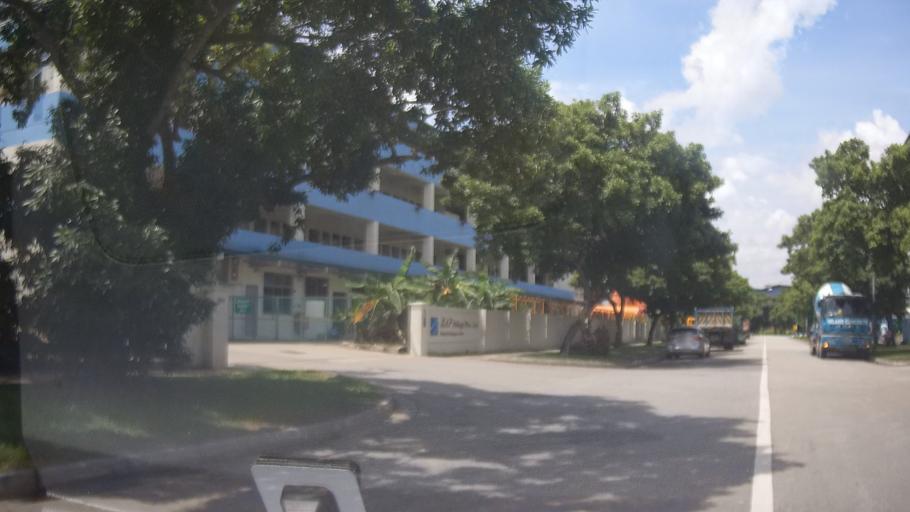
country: MY
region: Johor
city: Johor Bahru
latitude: 1.4345
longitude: 103.7462
